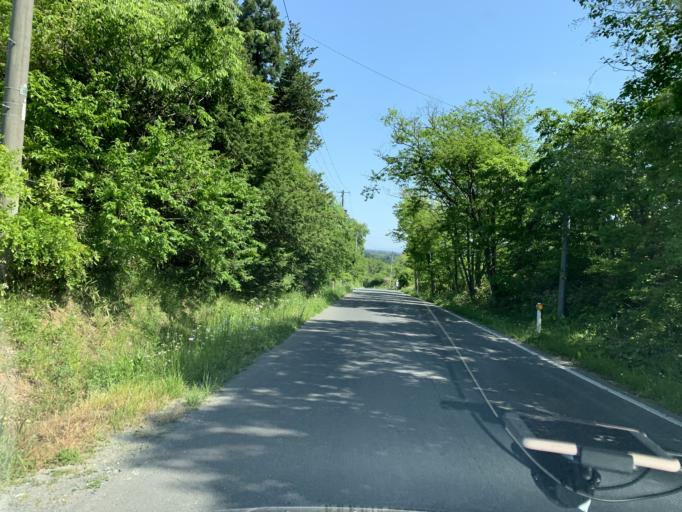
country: JP
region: Iwate
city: Mizusawa
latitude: 39.0539
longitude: 141.0647
